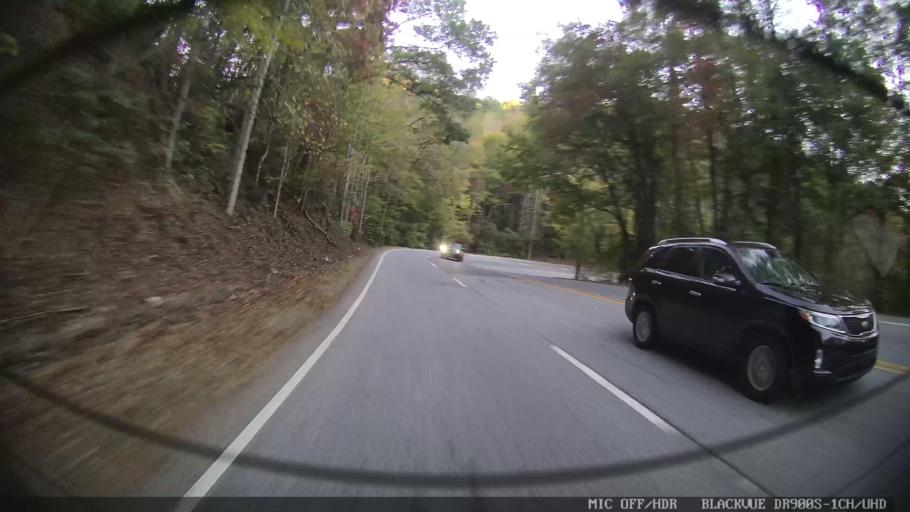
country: US
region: Georgia
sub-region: Union County
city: Blairsville
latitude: 34.7094
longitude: -83.9134
